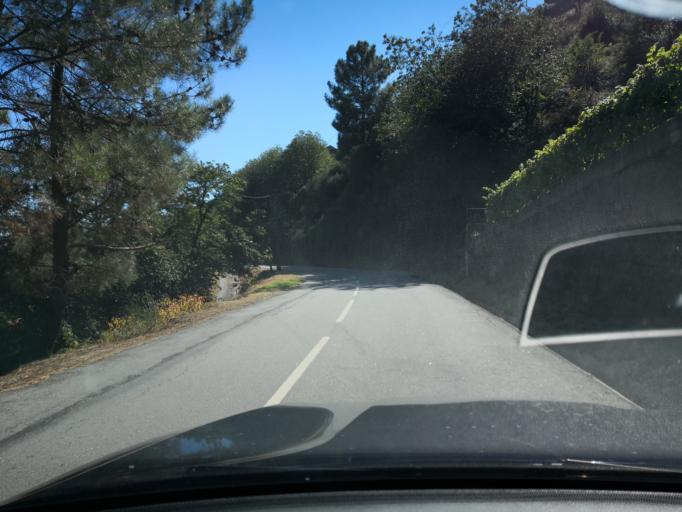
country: PT
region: Vila Real
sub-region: Santa Marta de Penaguiao
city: Santa Marta de Penaguiao
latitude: 41.2310
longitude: -7.7936
